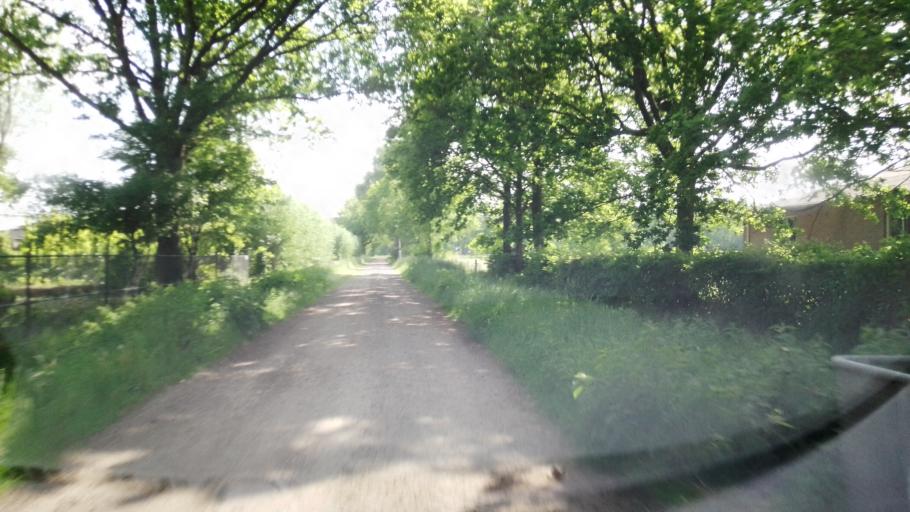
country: NL
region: Limburg
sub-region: Gemeente Peel en Maas
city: Maasbree
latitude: 51.4118
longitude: 6.0581
